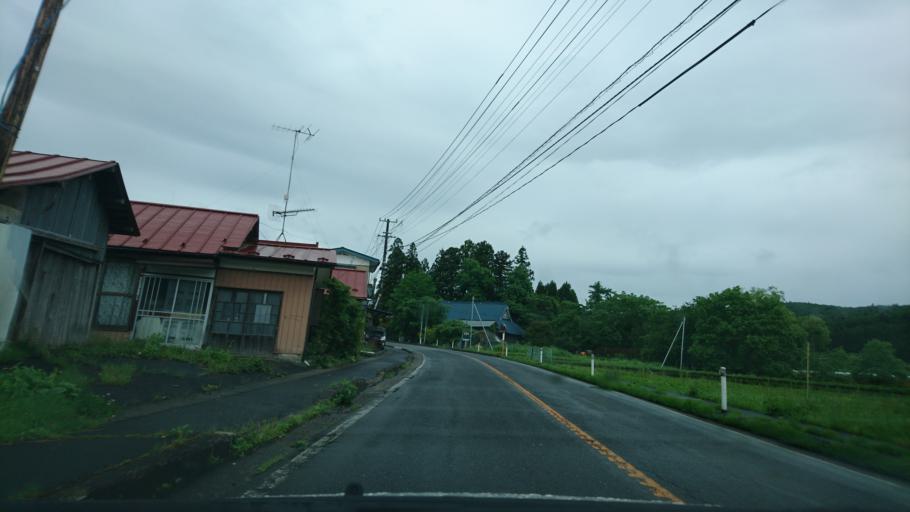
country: JP
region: Iwate
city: Ichinoseki
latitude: 38.9698
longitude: 140.9977
